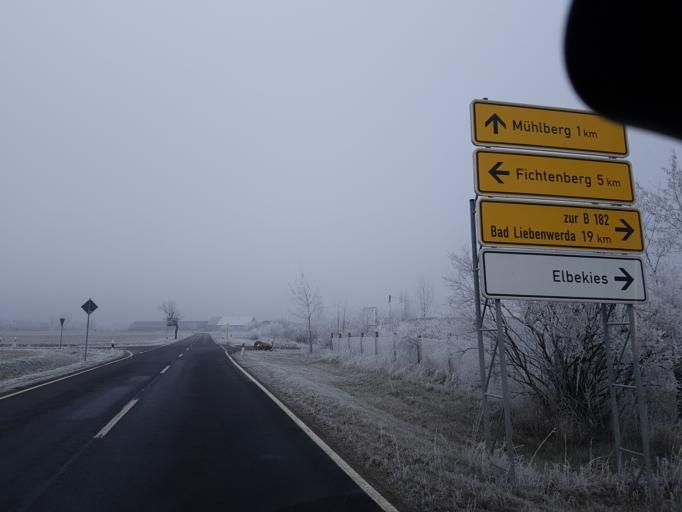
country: DE
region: Brandenburg
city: Muhlberg
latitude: 51.4302
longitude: 13.2360
